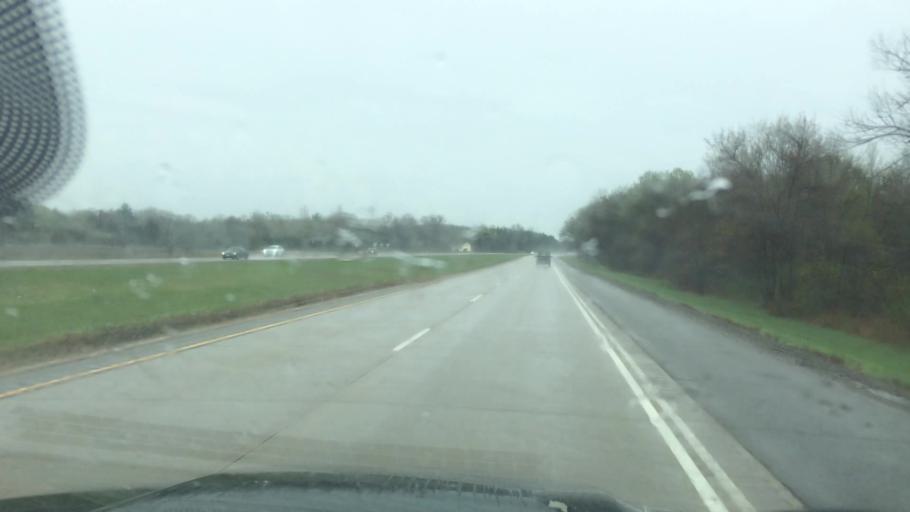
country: US
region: Wisconsin
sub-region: Portage County
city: Stevens Point
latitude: 44.6481
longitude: -89.6378
